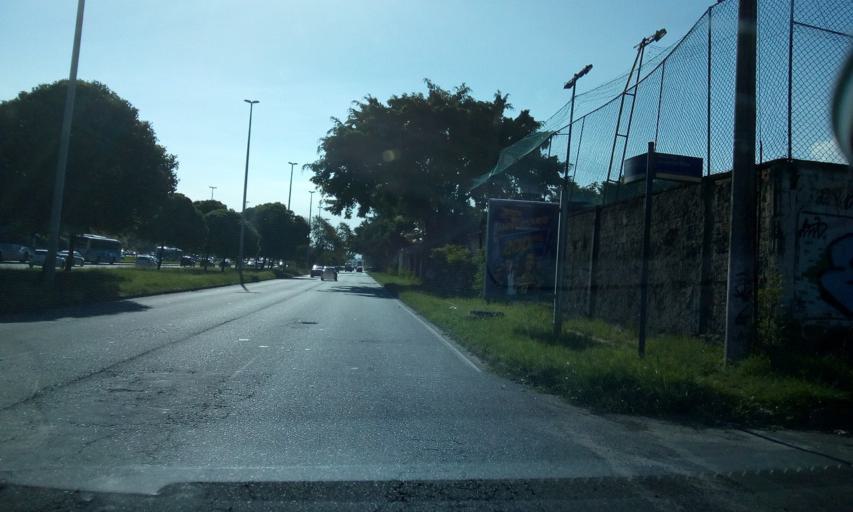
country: BR
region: Rio de Janeiro
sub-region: Nilopolis
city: Nilopolis
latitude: -23.0001
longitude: -43.3905
